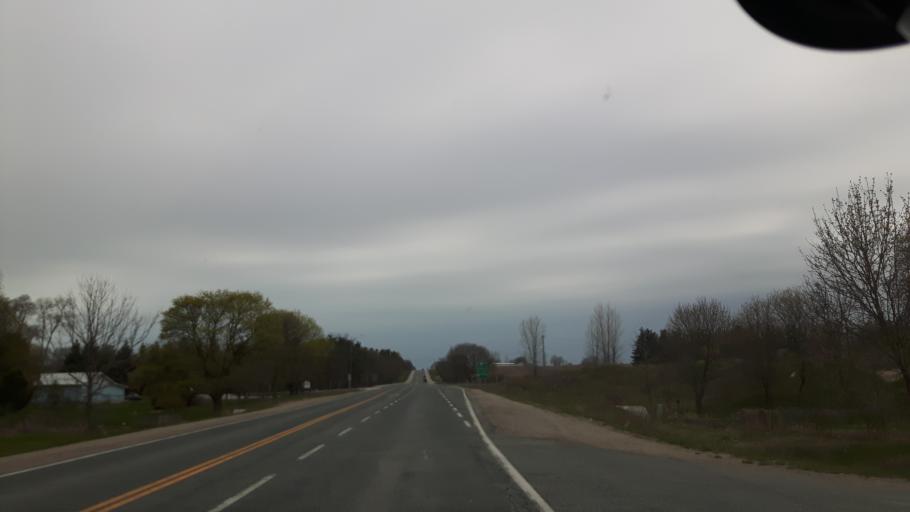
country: CA
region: Ontario
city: Goderich
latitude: 43.6455
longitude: -81.5998
